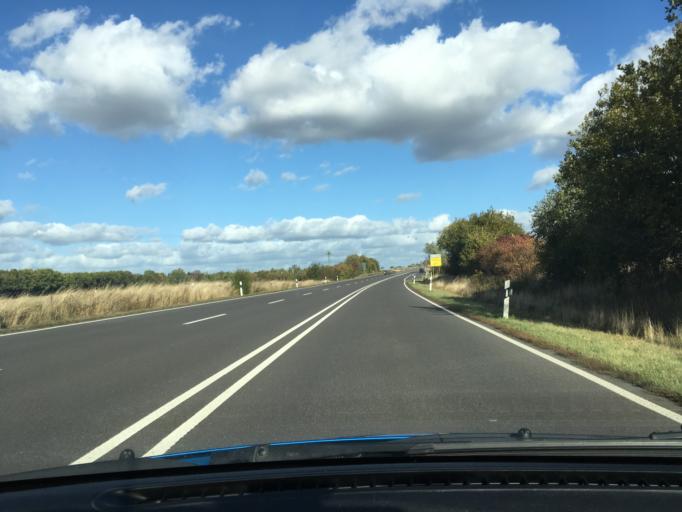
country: DE
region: Brandenburg
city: Perleberg
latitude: 53.0875
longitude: 11.8383
